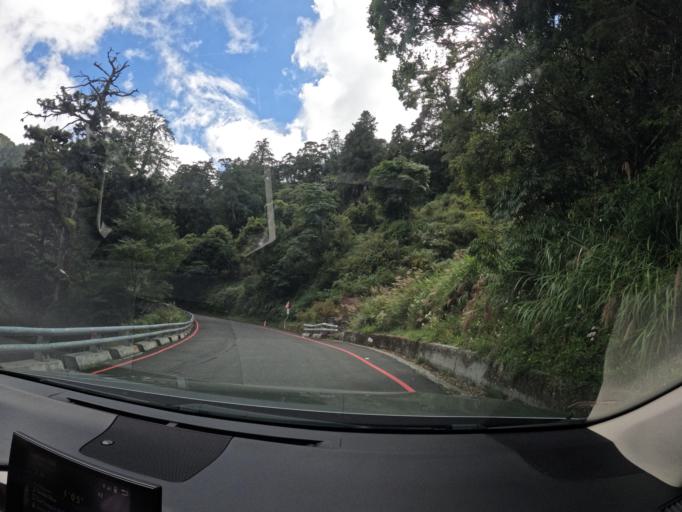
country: TW
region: Taiwan
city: Yujing
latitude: 23.2637
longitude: 120.9408
